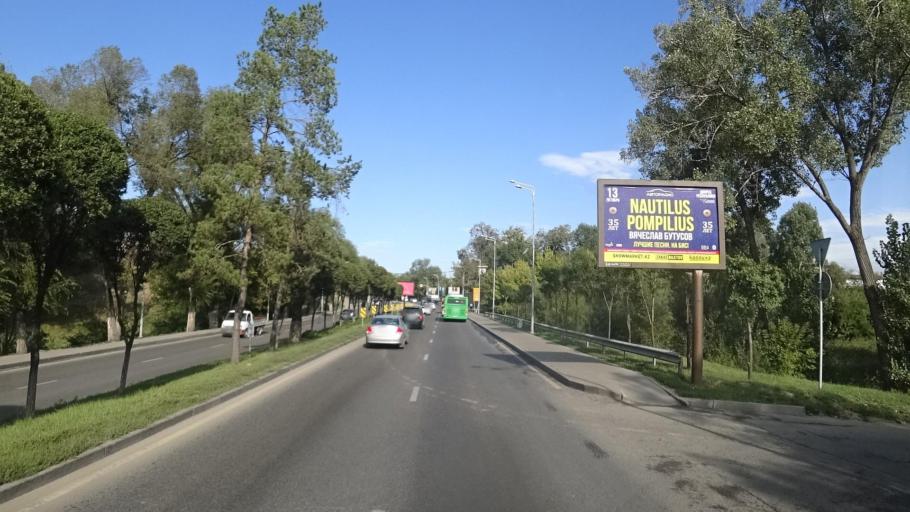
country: KZ
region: Almaty Oblysy
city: Pervomayskiy
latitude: 43.3435
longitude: 76.9980
